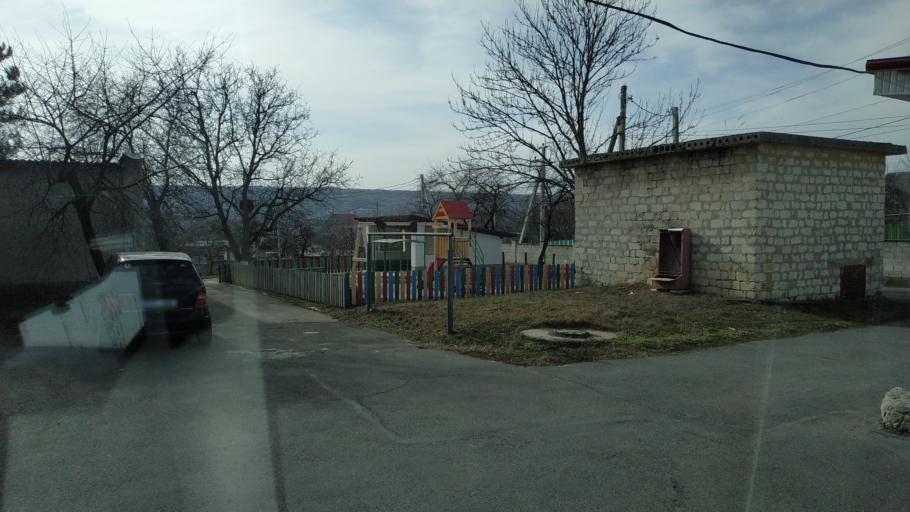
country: MD
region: Chisinau
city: Vatra
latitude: 47.0749
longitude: 28.6937
